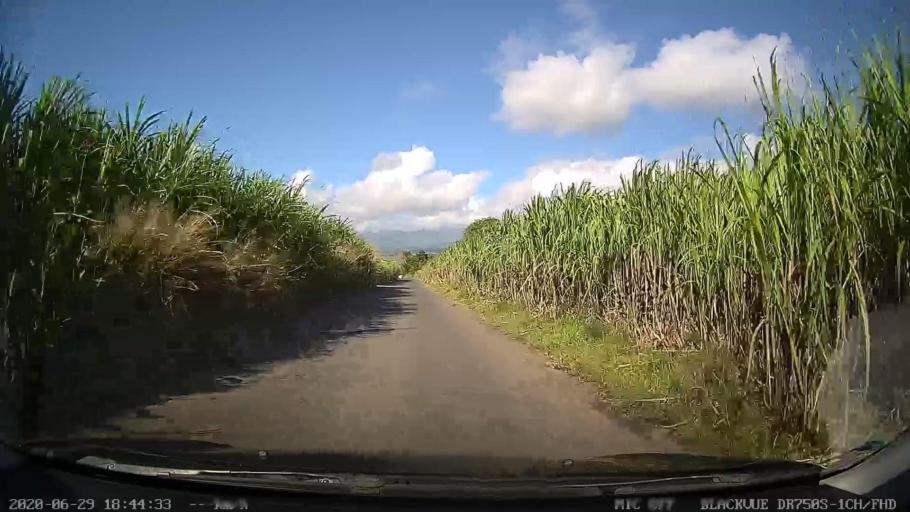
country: RE
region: Reunion
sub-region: Reunion
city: Bras-Panon
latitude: -20.9951
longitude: 55.6857
